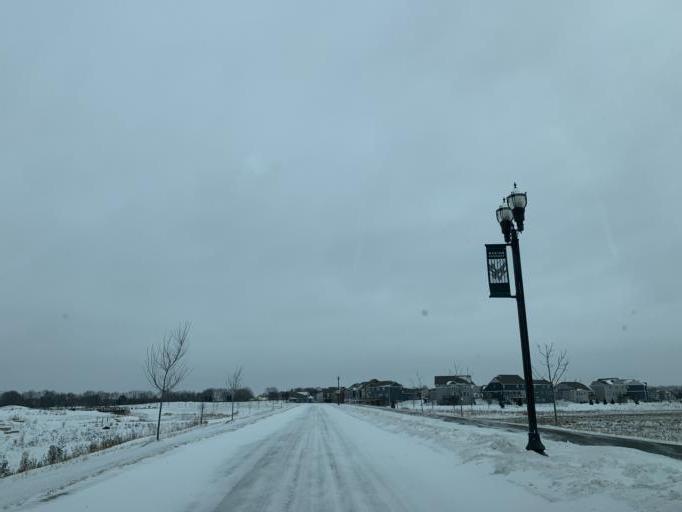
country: US
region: Minnesota
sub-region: Washington County
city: Cottage Grove
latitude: 44.8548
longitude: -92.9157
